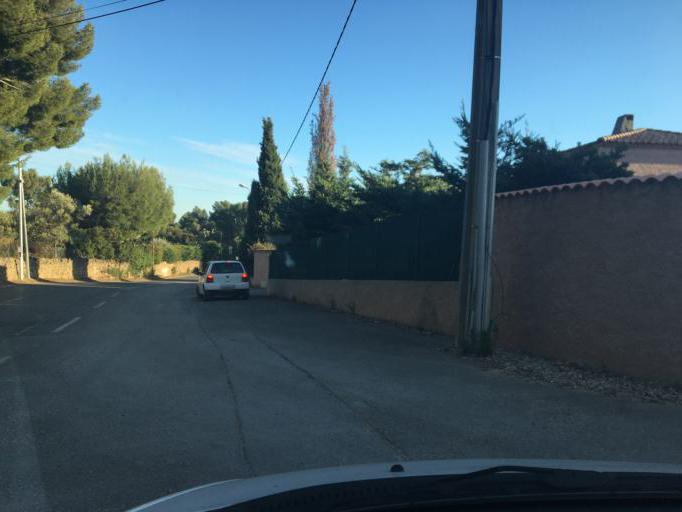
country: FR
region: Provence-Alpes-Cote d'Azur
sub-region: Departement des Bouches-du-Rhone
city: Ceyreste
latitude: 43.2034
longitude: 5.6053
